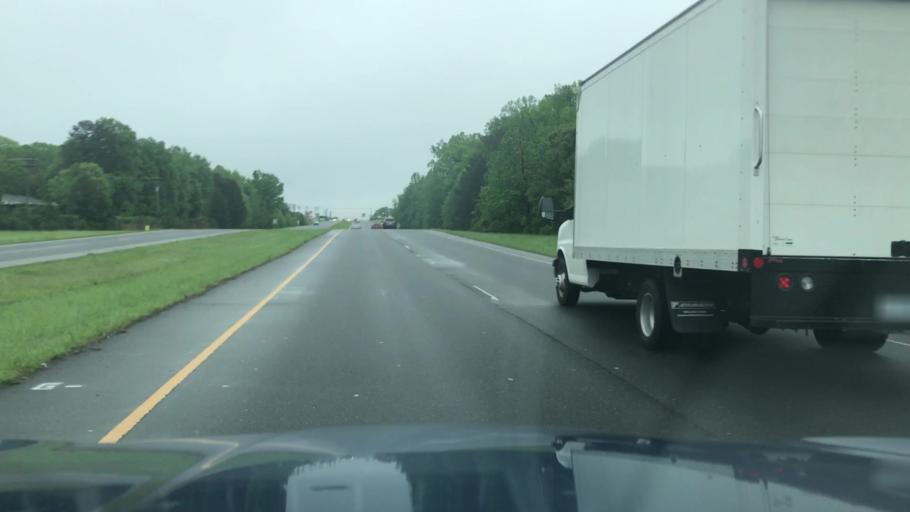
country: US
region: North Carolina
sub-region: Mecklenburg County
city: Matthews
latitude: 35.1242
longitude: -80.7037
